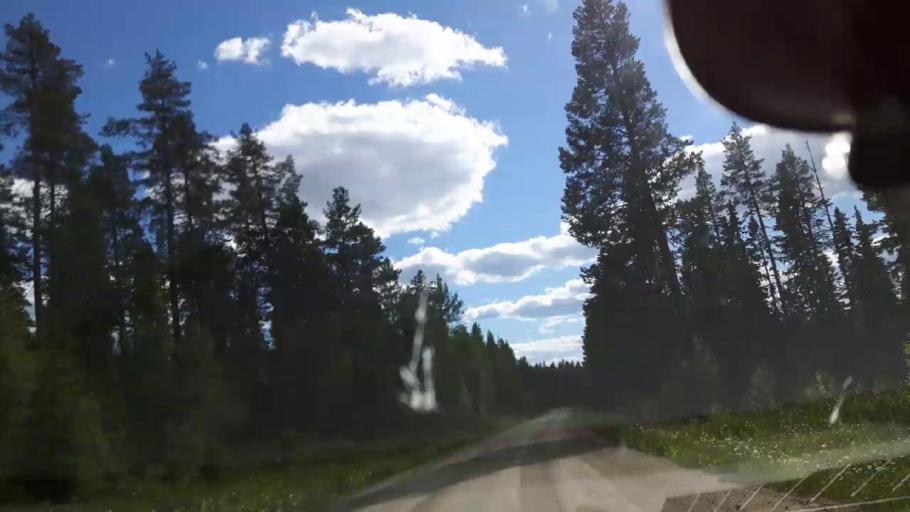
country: SE
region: Vaesternorrland
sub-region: Ange Kommun
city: Ange
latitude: 62.7310
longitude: 15.6453
